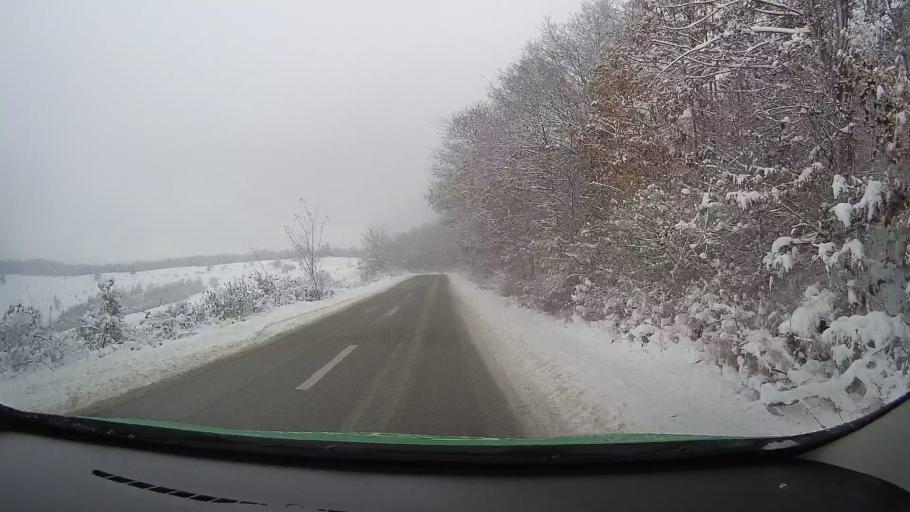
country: RO
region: Hunedoara
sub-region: Comuna Teliucu Inferior
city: Teliucu Inferior
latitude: 45.6848
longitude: 22.9096
